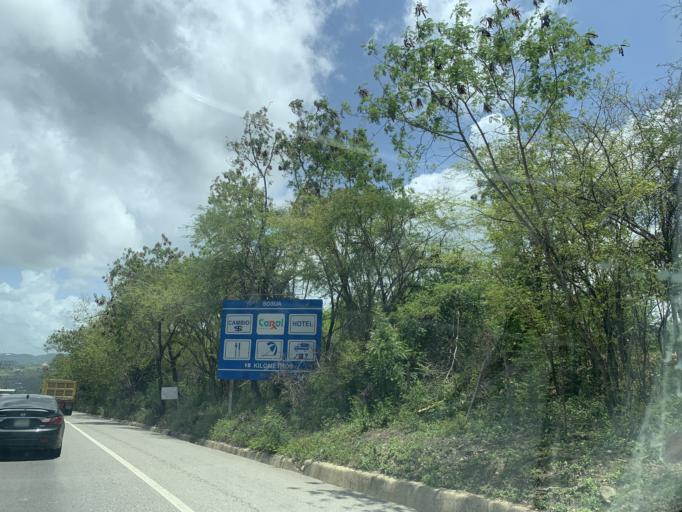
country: DO
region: Puerto Plata
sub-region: Puerto Plata
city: Puerto Plata
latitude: 19.7269
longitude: -70.6240
